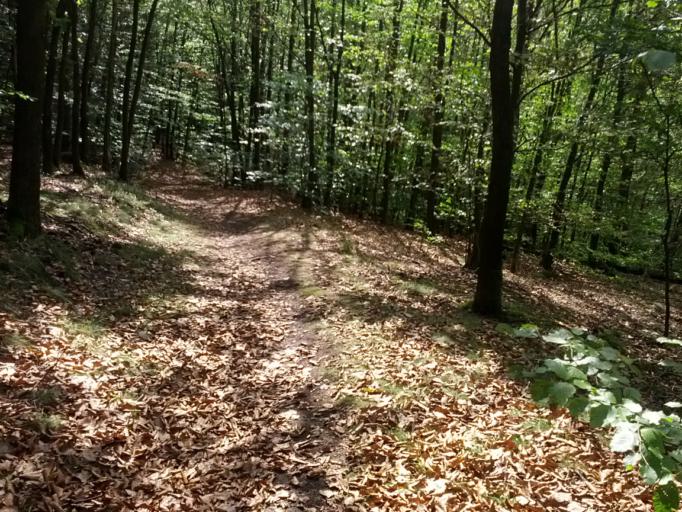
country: DE
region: Thuringia
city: Eisenach
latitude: 50.9562
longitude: 10.3160
